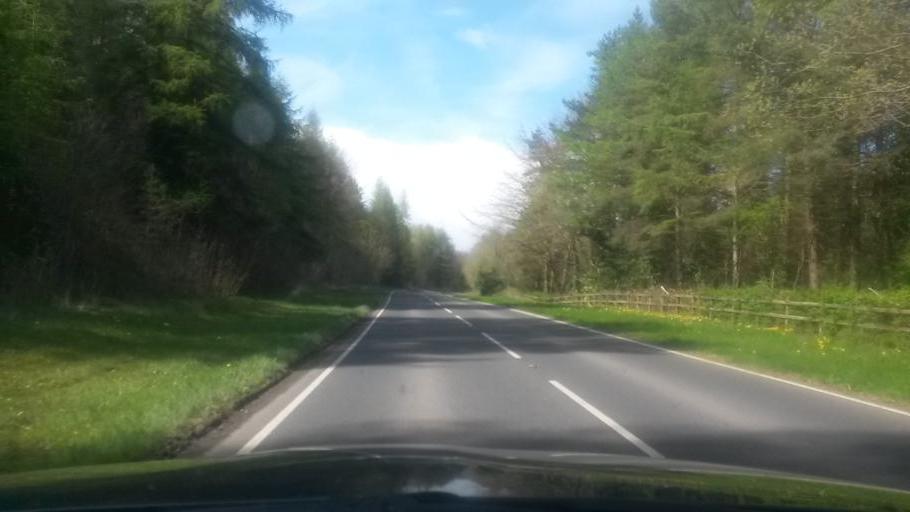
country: GB
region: Northern Ireland
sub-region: Fermanagh District
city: Enniskillen
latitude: 54.3797
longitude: -7.6894
